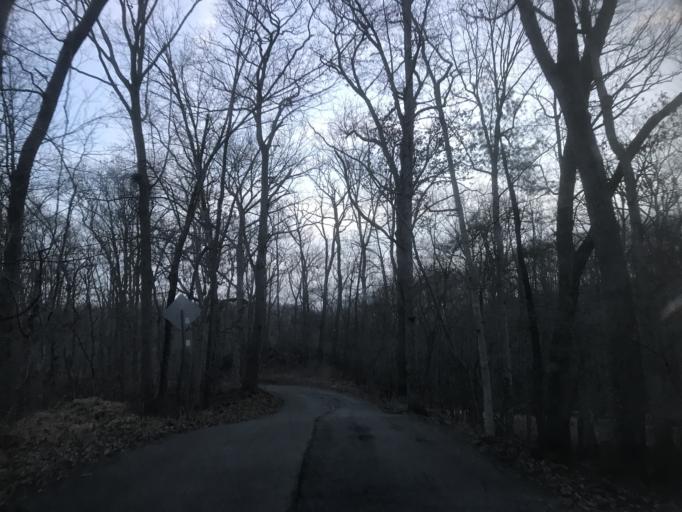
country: US
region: Pennsylvania
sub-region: York County
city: New Freedom
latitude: 39.6796
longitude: -76.7024
